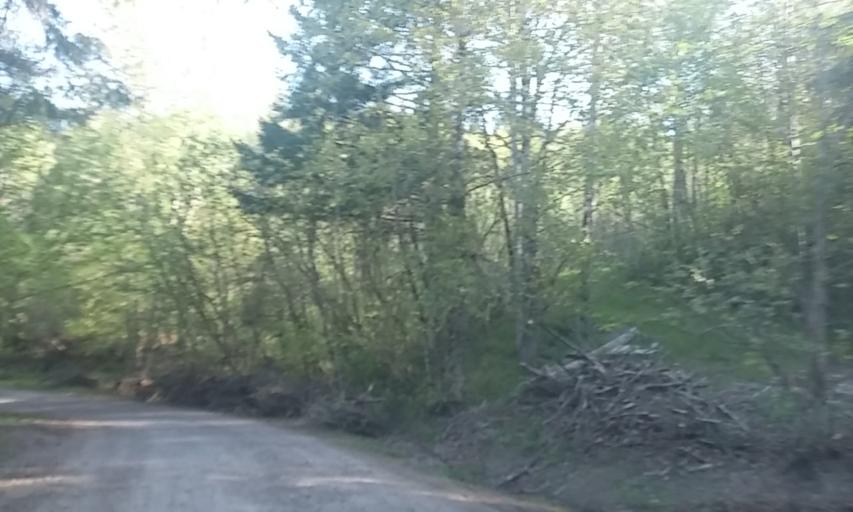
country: US
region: Oregon
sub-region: Washington County
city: Cedar Mill
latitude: 45.5518
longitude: -122.7872
